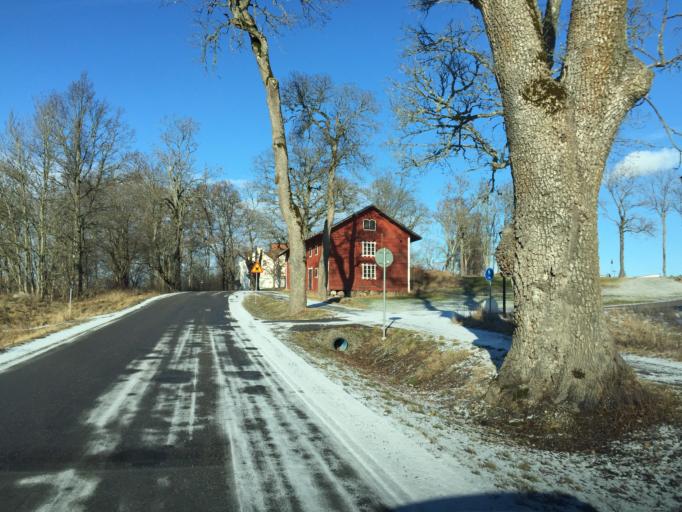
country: SE
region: Stockholm
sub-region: Nykvarns Kommun
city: Nykvarn
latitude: 59.1991
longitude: 17.4401
